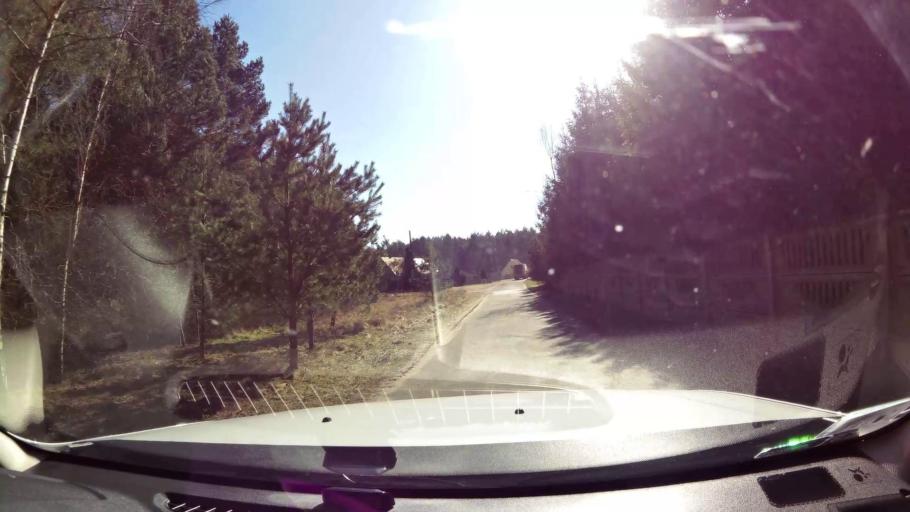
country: PL
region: West Pomeranian Voivodeship
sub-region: Powiat gryfinski
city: Banie
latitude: 53.0347
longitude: 14.6316
